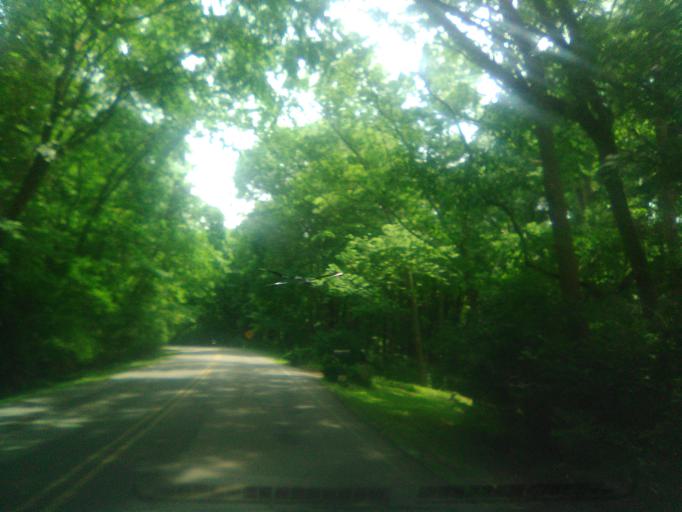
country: US
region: Tennessee
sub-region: Davidson County
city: Forest Hills
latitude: 36.0761
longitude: -86.8548
